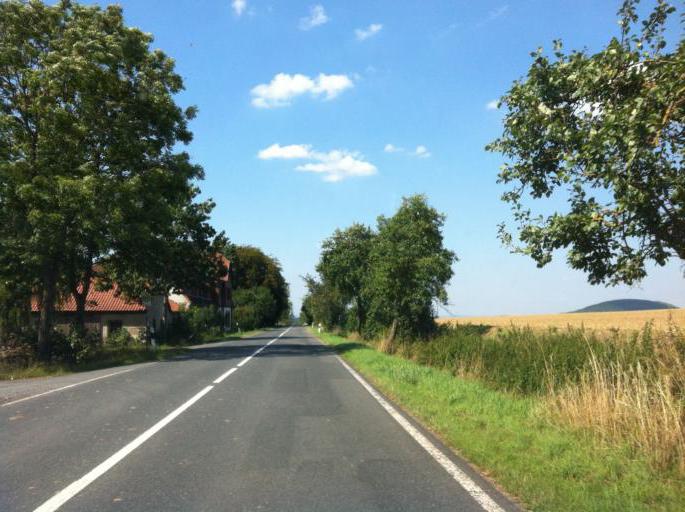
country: DE
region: Thuringia
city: Freienhagen
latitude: 51.4304
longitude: 10.0779
